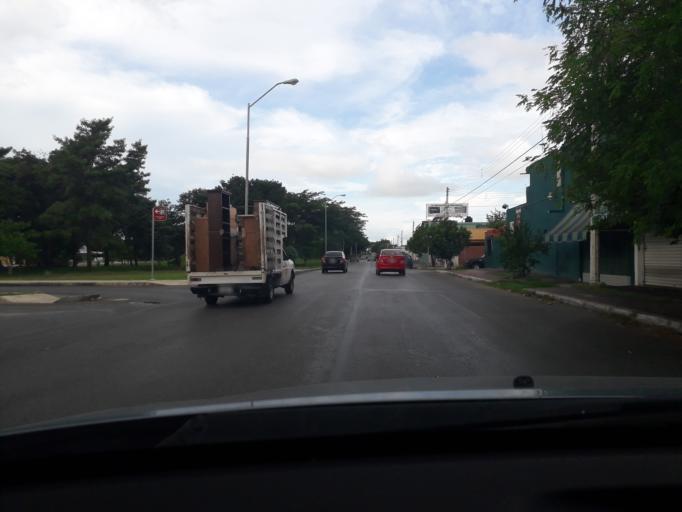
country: MX
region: Yucatan
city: Merida
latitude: 20.9794
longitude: -89.6633
